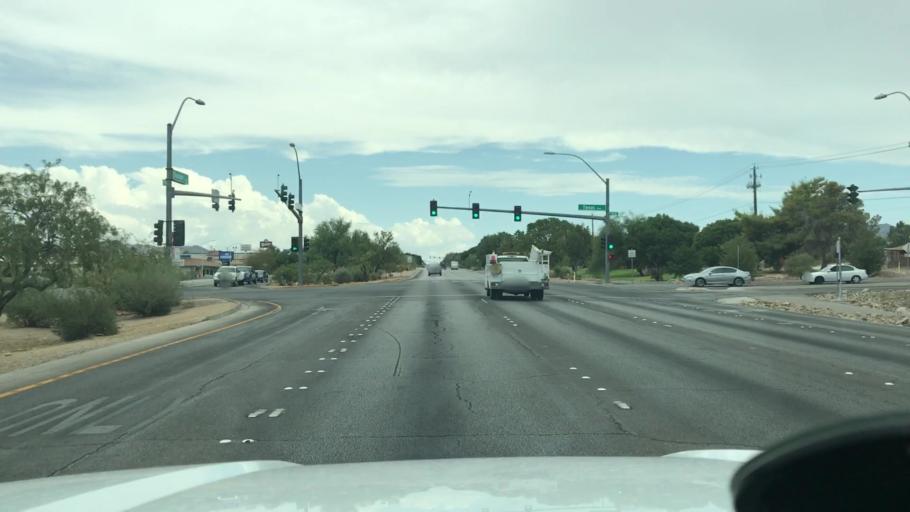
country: US
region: Nevada
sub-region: Clark County
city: Henderson
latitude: 36.0370
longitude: -114.9793
